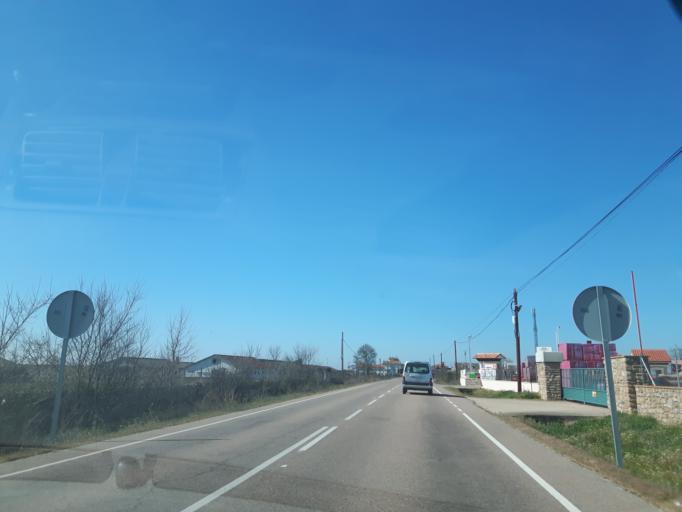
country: ES
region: Castille and Leon
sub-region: Provincia de Salamanca
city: Lumbrales
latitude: 40.9390
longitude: -6.7062
